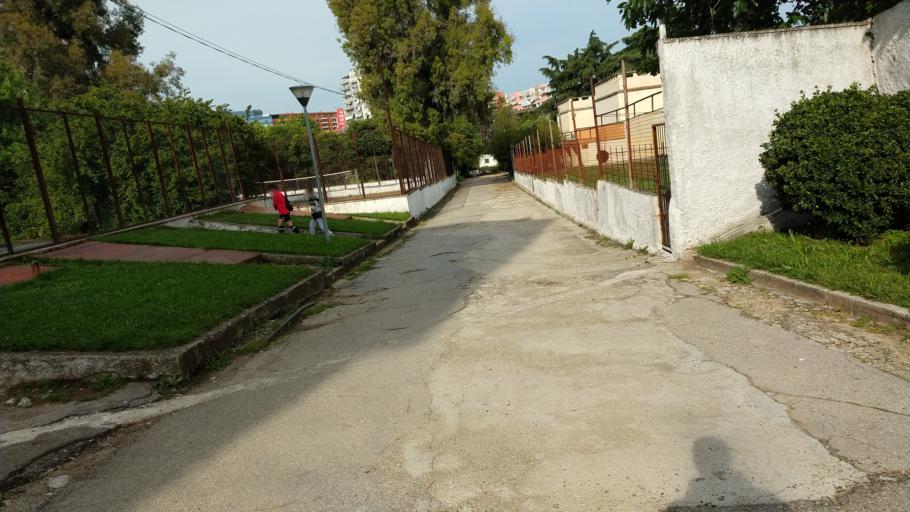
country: AL
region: Tirane
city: Tirana
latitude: 41.3353
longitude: 19.8090
